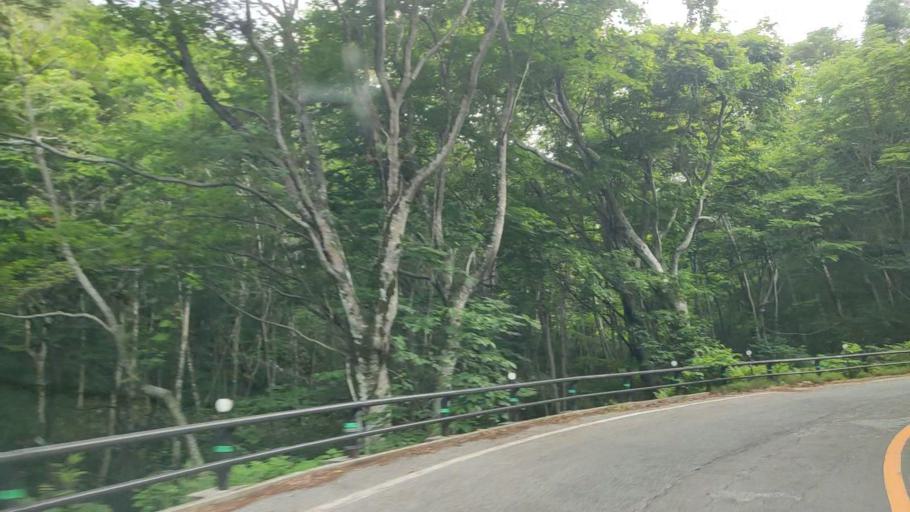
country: JP
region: Tottori
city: Yonago
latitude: 35.3473
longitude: 133.5534
